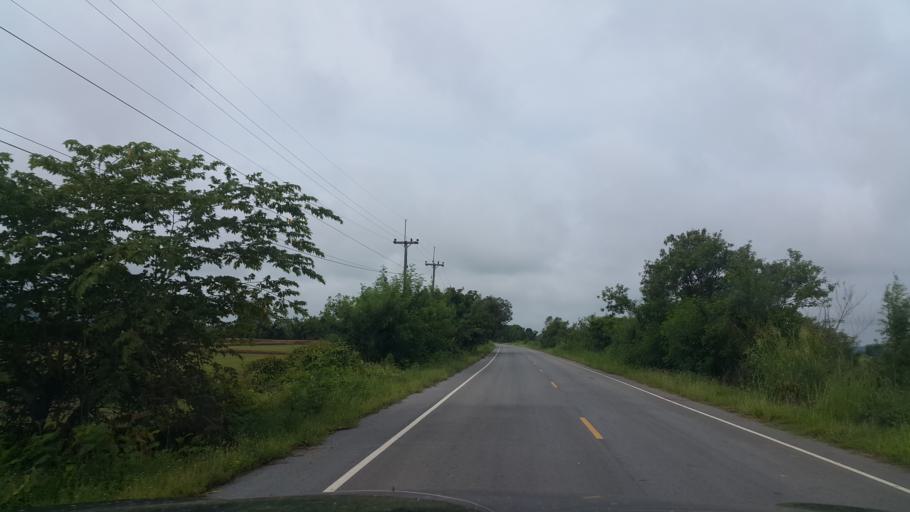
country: TH
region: Sukhothai
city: Sawankhalok
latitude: 17.3115
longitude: 99.6988
